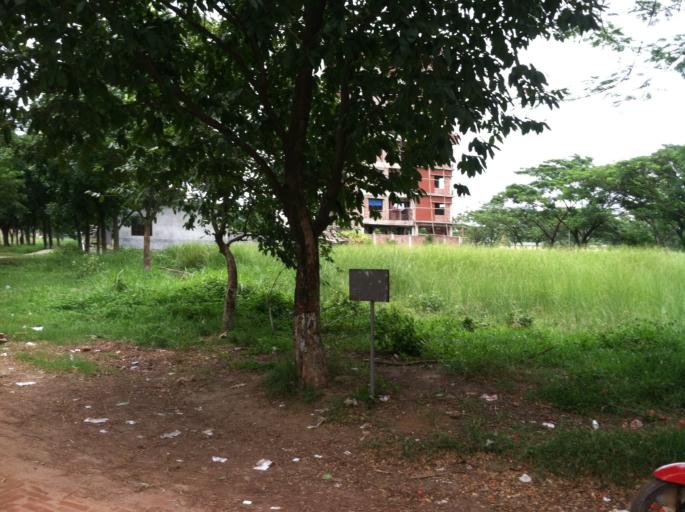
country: BD
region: Dhaka
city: Paltan
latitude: 23.7277
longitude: 90.4488
